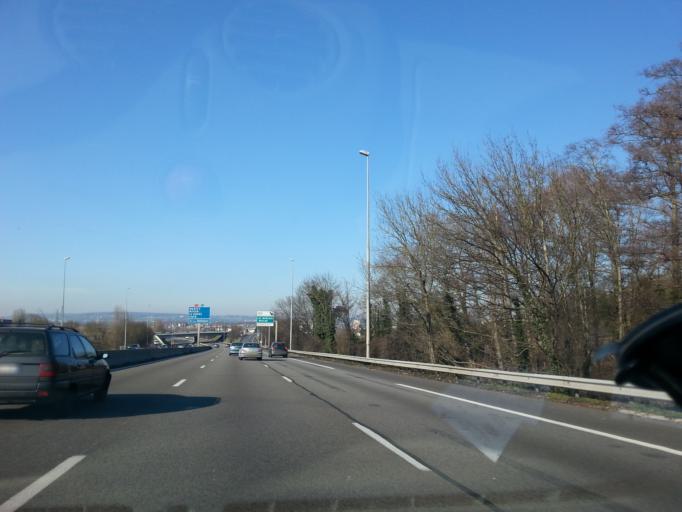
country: FR
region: Ile-de-France
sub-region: Departement des Yvelines
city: Chapet
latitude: 48.9636
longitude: 1.9268
